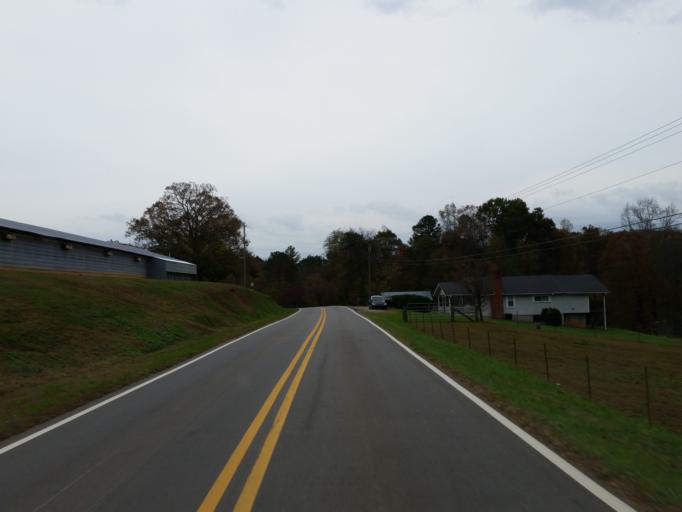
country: US
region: Georgia
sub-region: Gilmer County
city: Ellijay
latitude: 34.6481
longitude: -84.3479
